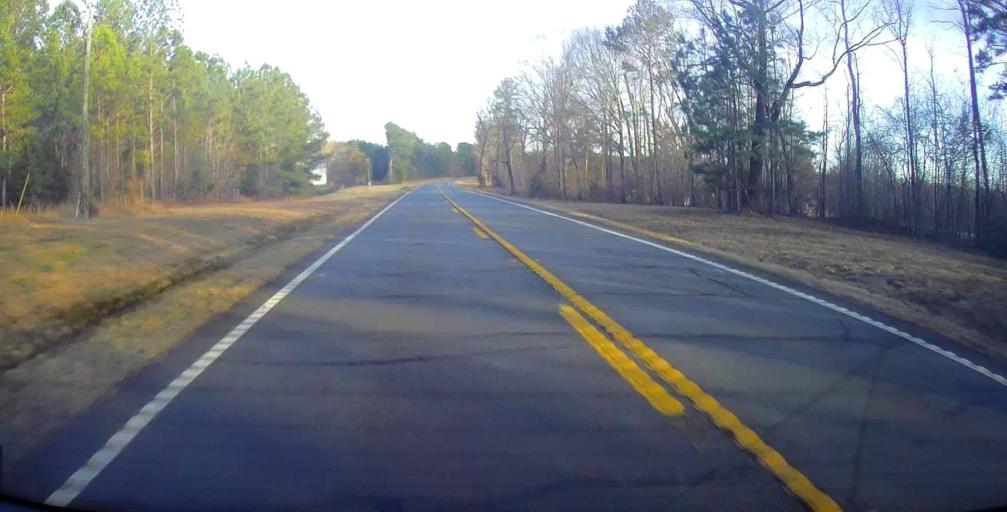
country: US
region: Georgia
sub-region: Talbot County
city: Sardis
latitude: 32.7912
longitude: -84.5374
